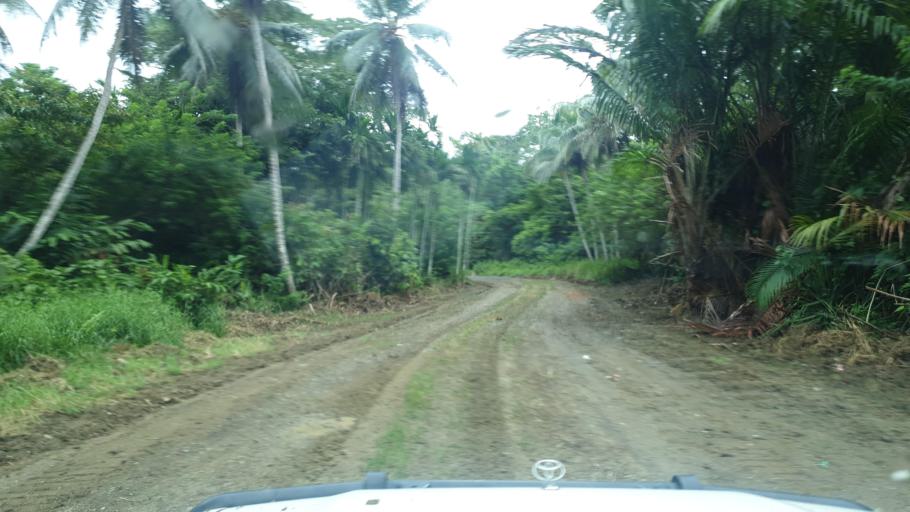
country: PG
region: Gulf
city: Kerema
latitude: -7.9586
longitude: 145.8407
